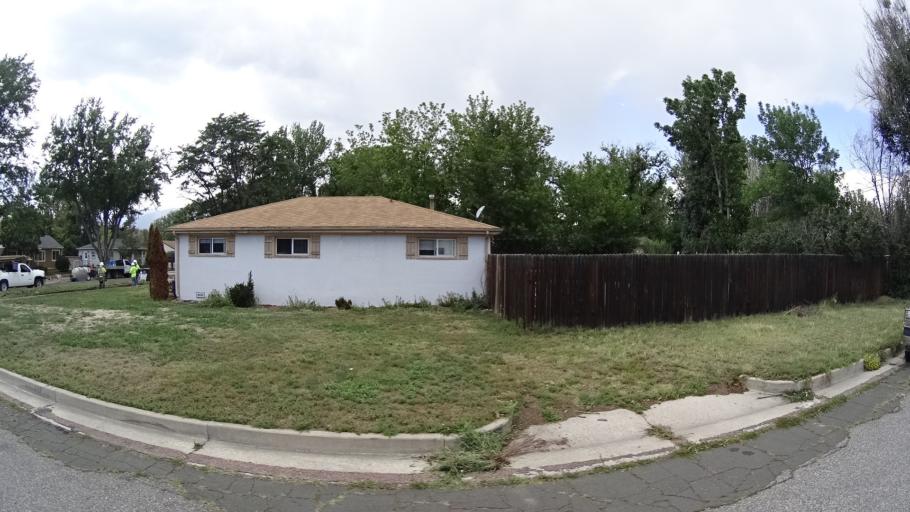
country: US
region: Colorado
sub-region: El Paso County
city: Colorado Springs
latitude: 38.8631
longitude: -104.8052
